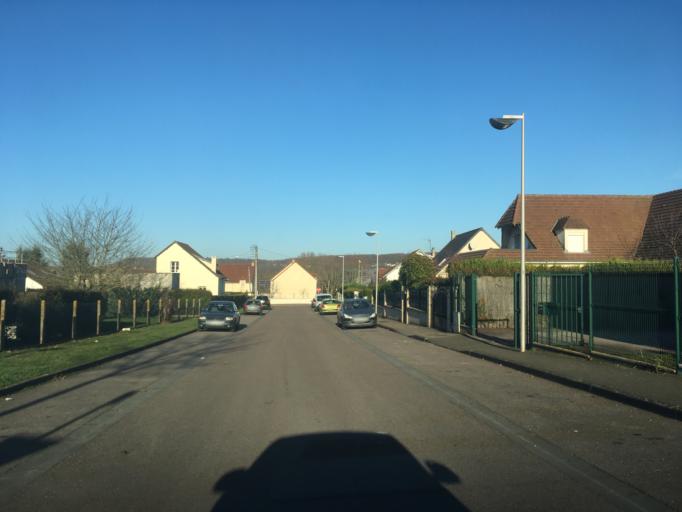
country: FR
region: Haute-Normandie
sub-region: Departement de l'Eure
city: Vernon
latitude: 49.0802
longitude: 1.4869
